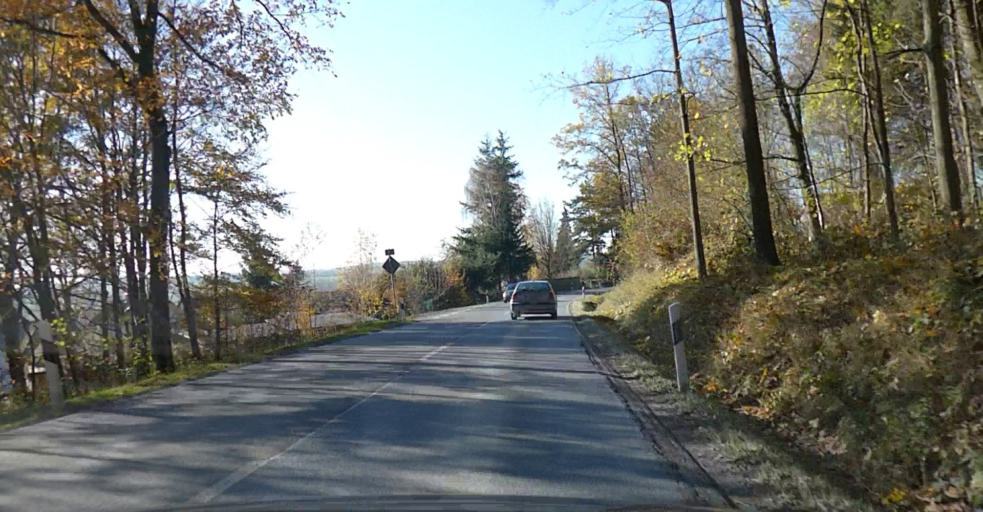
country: DE
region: Bavaria
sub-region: Upper Franconia
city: Kupferberg
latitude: 50.1300
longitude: 11.5604
